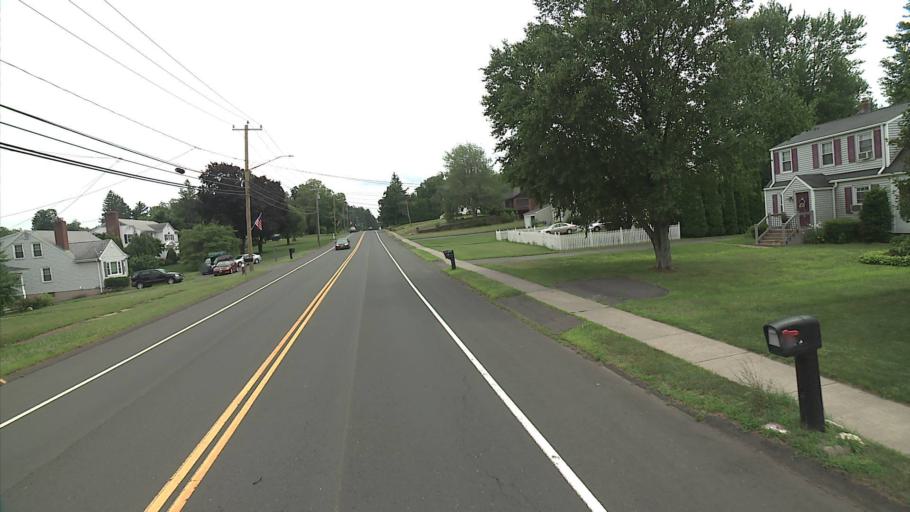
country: US
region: Connecticut
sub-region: Middlesex County
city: Cromwell
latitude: 41.6123
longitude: -72.6519
